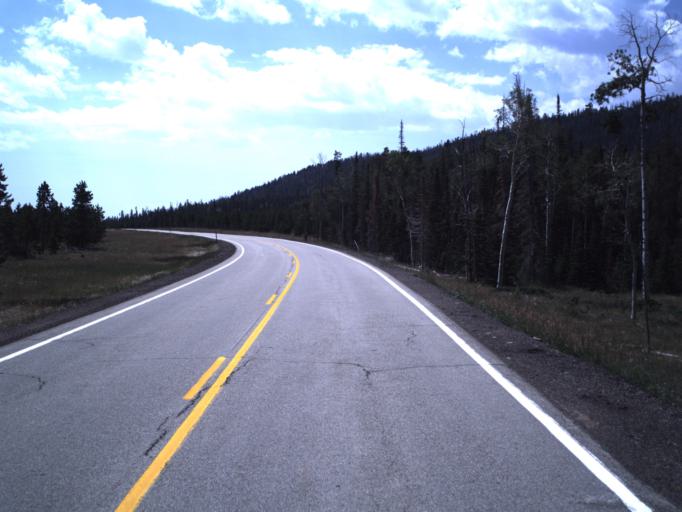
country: US
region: Utah
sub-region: Uintah County
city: Maeser
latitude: 40.7493
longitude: -109.4722
